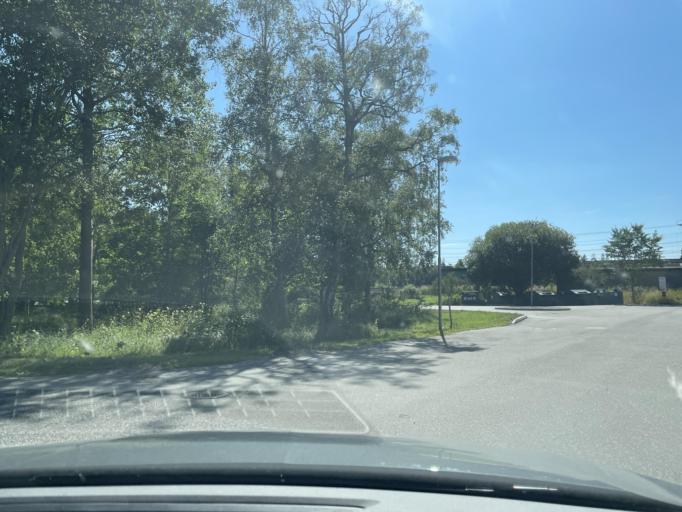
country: SE
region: Stockholm
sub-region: Sigtuna Kommun
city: Rosersberg
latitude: 59.5836
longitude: 17.8819
